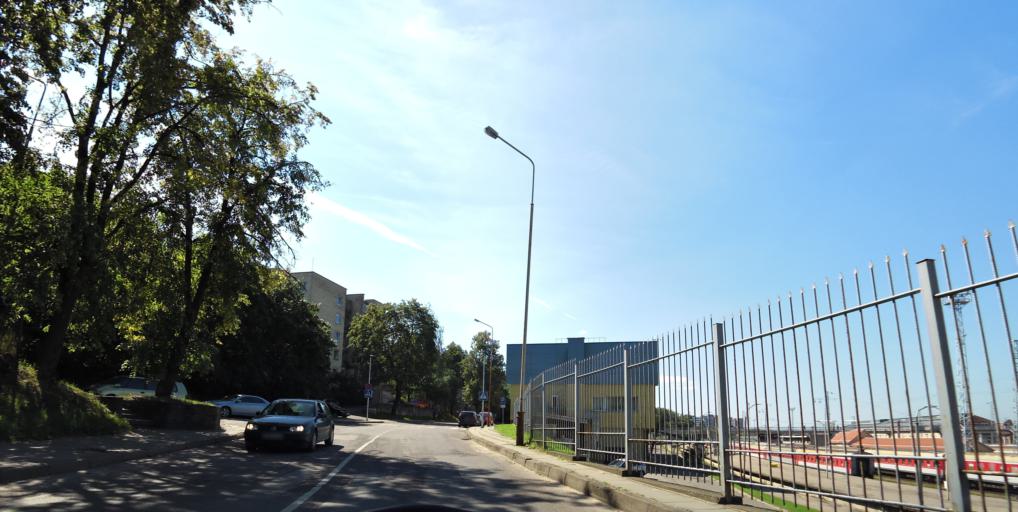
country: LT
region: Vilnius County
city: Naujamiestis
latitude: 54.6691
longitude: 25.2861
